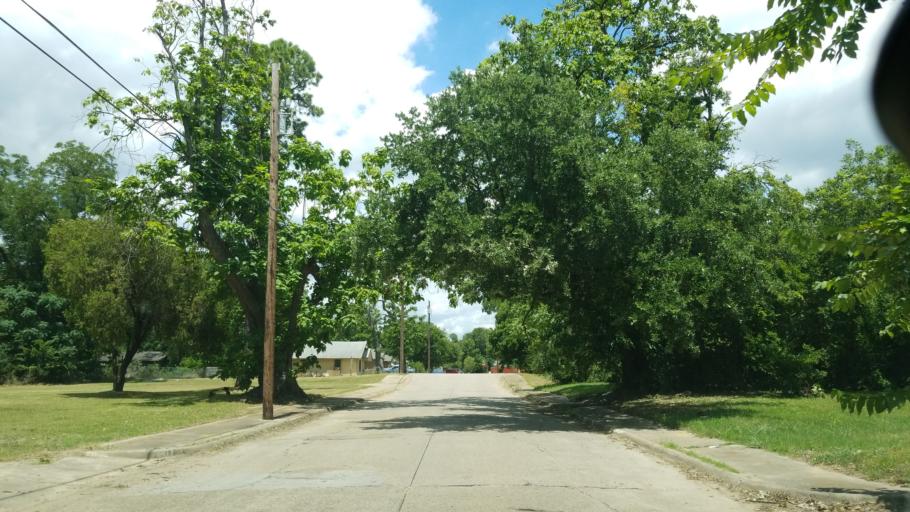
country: US
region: Texas
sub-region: Dallas County
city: Dallas
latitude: 32.7400
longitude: -96.7549
